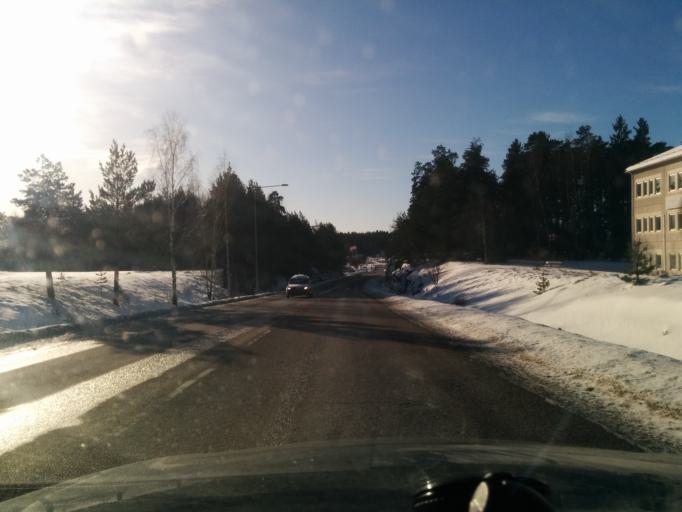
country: SE
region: Stockholm
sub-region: Taby Kommun
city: Taby
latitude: 59.4653
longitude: 18.1365
